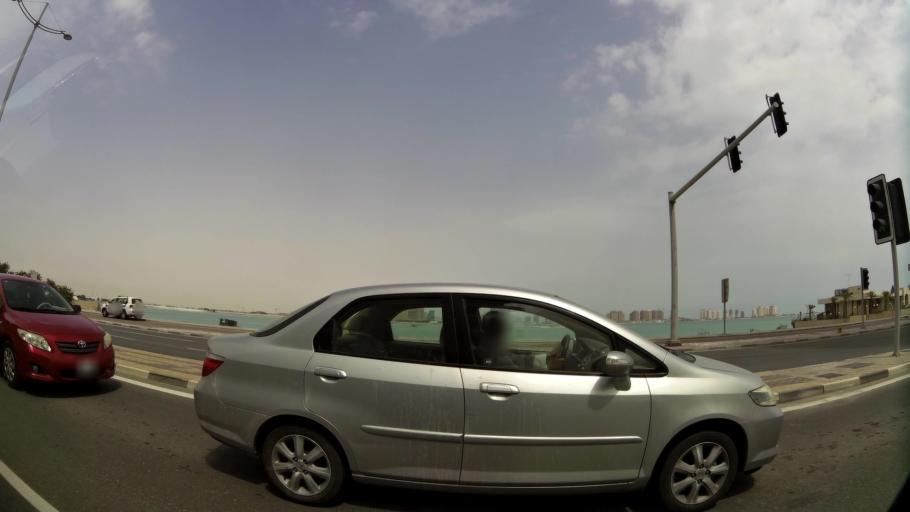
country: QA
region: Baladiyat ad Dawhah
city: Doha
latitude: 25.3310
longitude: 51.5348
